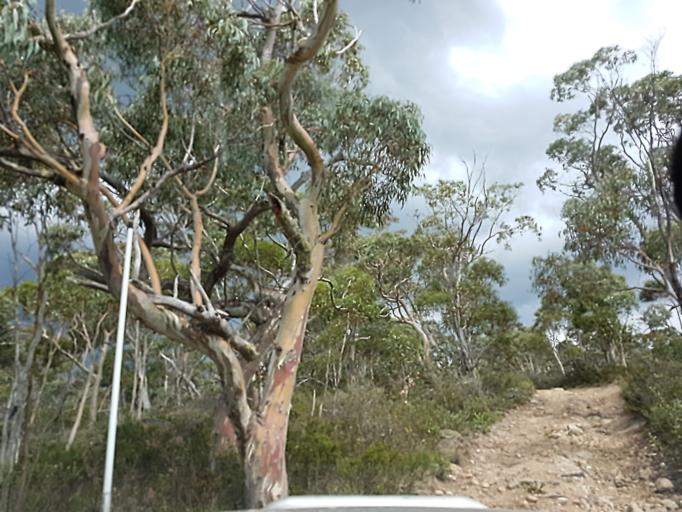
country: AU
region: New South Wales
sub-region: Snowy River
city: Jindabyne
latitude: -36.8763
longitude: 148.1785
